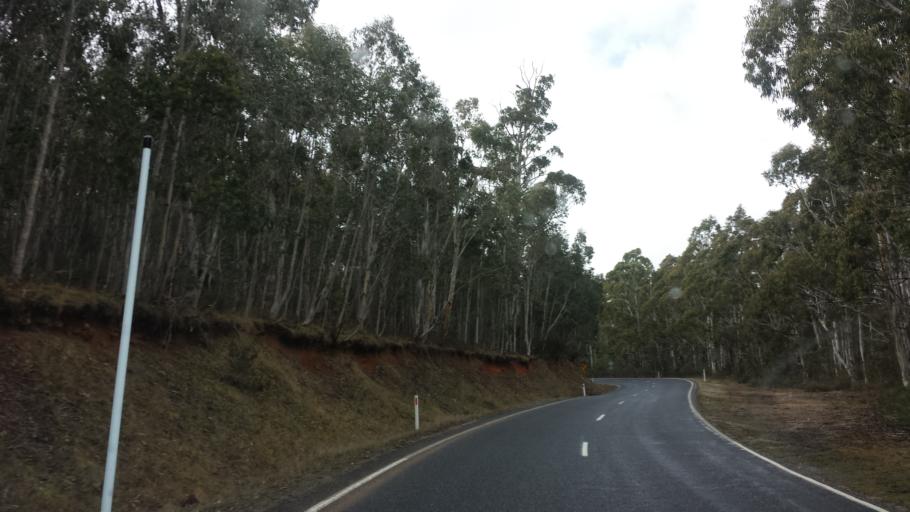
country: AU
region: Victoria
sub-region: Alpine
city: Mount Beauty
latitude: -37.1332
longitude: 147.5118
